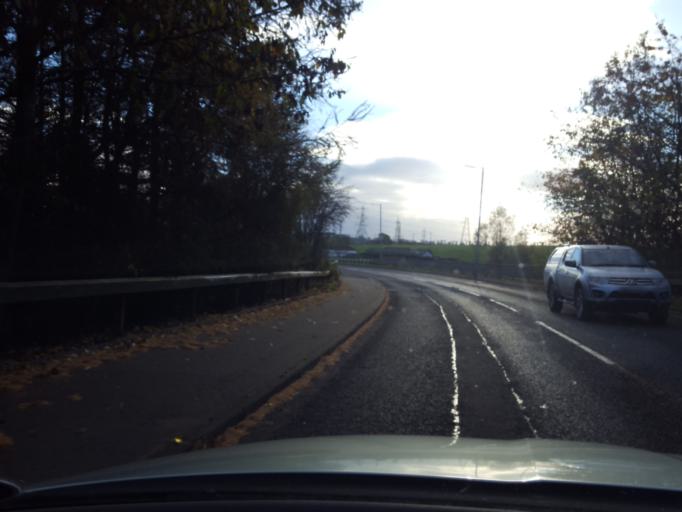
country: GB
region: Scotland
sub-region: North Lanarkshire
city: Chryston
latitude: 55.8847
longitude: -4.0821
